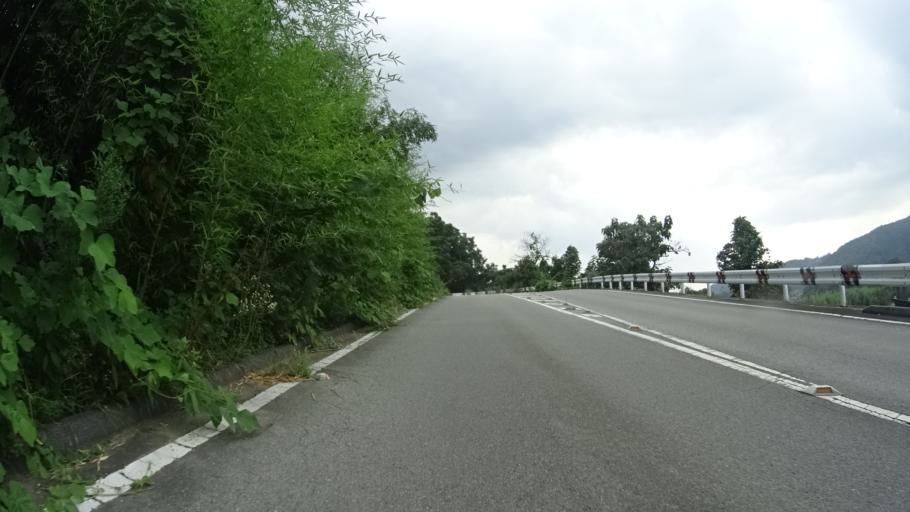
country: JP
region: Yamanashi
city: Enzan
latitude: 35.7436
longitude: 138.7224
